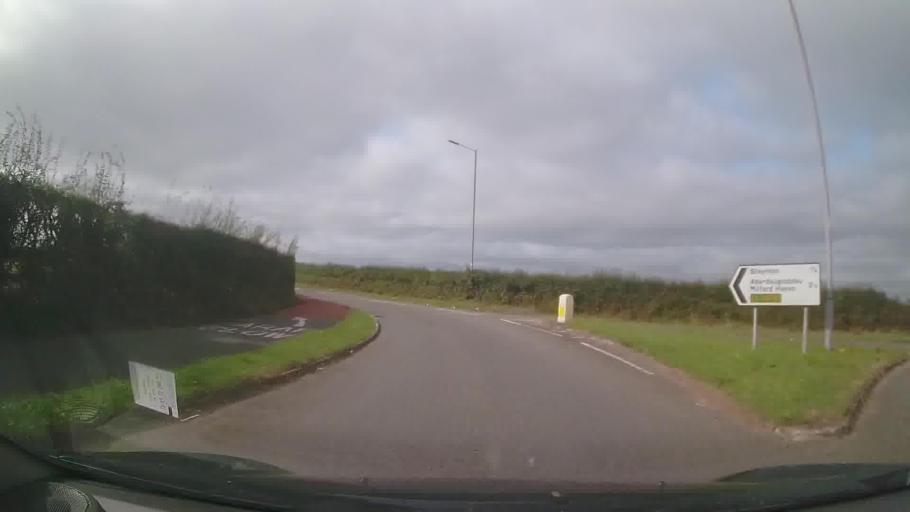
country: GB
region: Wales
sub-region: Pembrokeshire
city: Johnston
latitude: 51.7313
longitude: -4.9911
